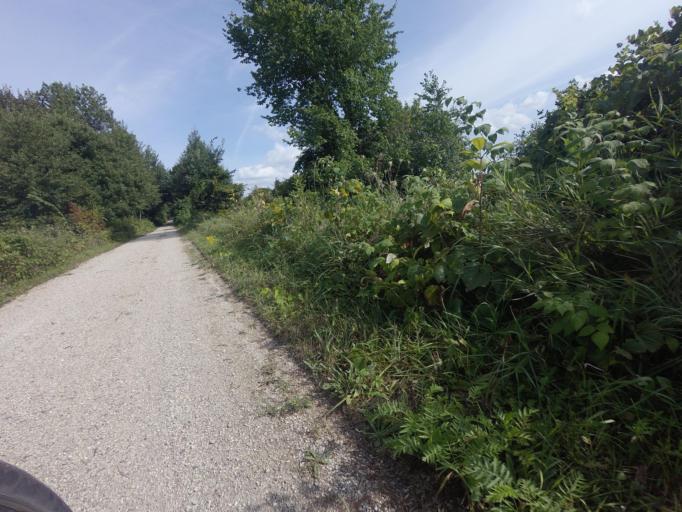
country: CA
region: Ontario
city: Waterloo
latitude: 43.5873
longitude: -80.4358
